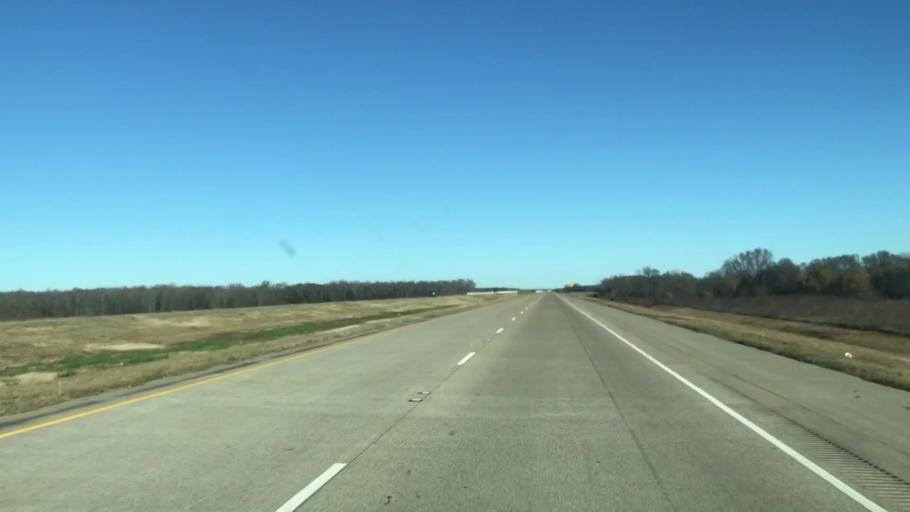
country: US
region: Louisiana
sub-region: Caddo Parish
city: Blanchard
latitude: 32.6195
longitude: -93.8354
